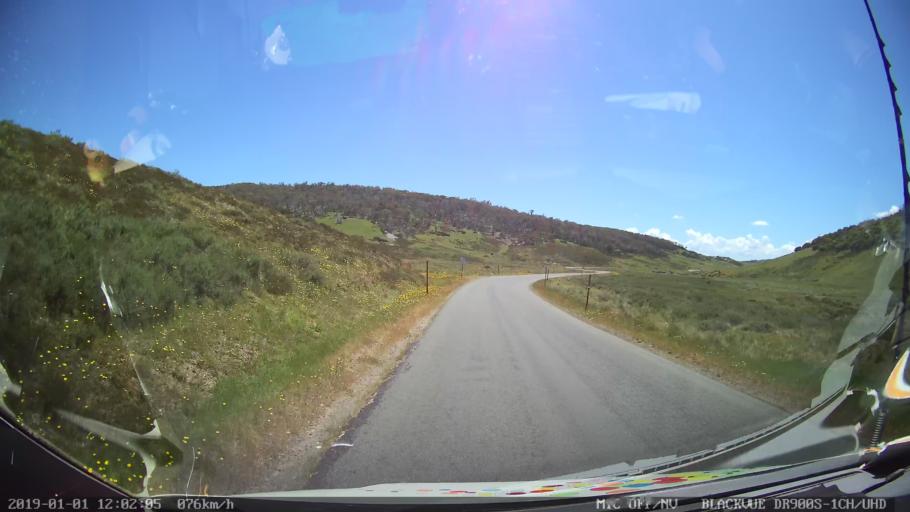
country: AU
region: New South Wales
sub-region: Snowy River
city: Jindabyne
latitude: -35.8749
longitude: 148.4738
